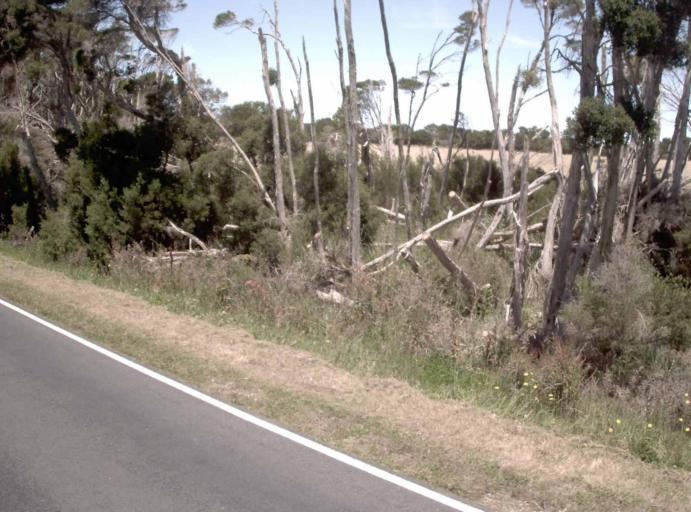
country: AU
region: Victoria
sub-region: Bass Coast
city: North Wonthaggi
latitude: -38.7753
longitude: 146.1616
